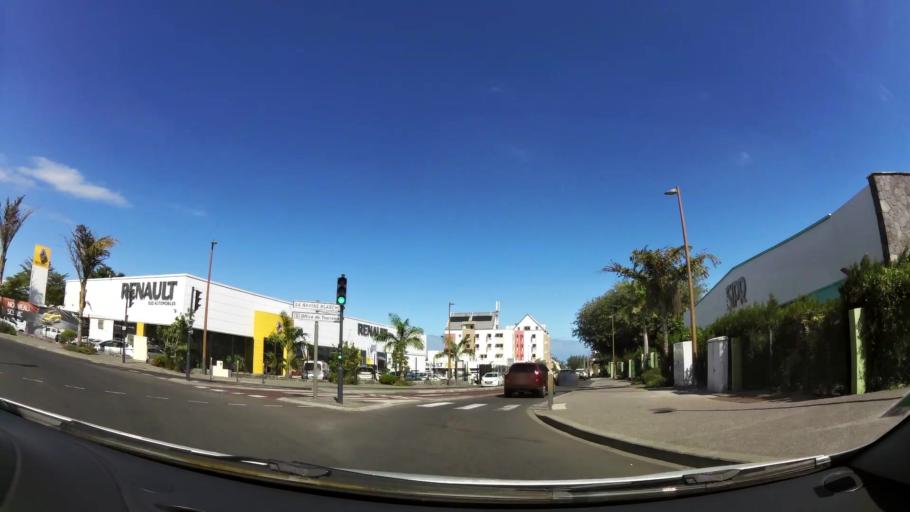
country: RE
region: Reunion
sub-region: Reunion
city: Saint-Pierre
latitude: -21.3338
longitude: 55.4602
